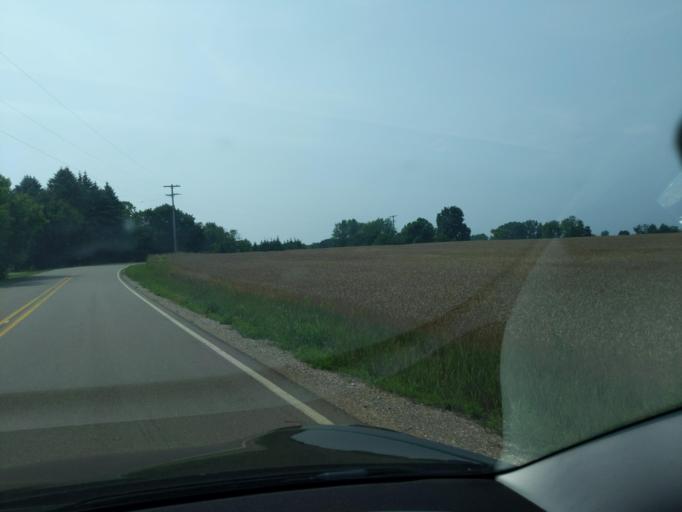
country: US
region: Michigan
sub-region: Clinton County
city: DeWitt
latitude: 42.9153
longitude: -84.5804
